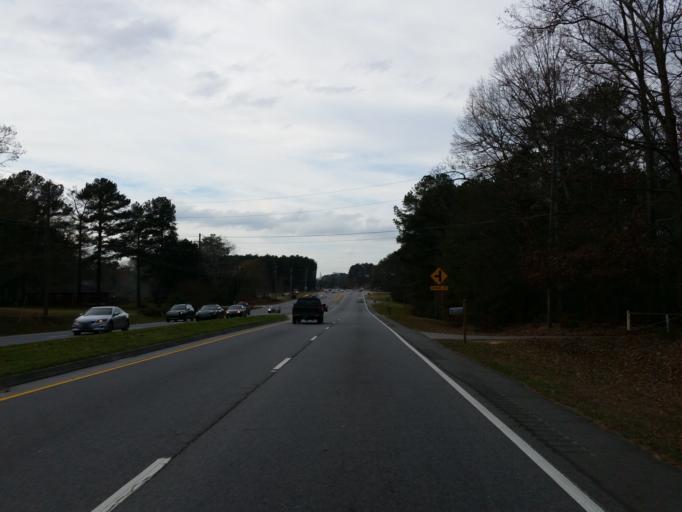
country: US
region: Georgia
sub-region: Cobb County
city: Powder Springs
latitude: 33.8981
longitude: -84.6543
